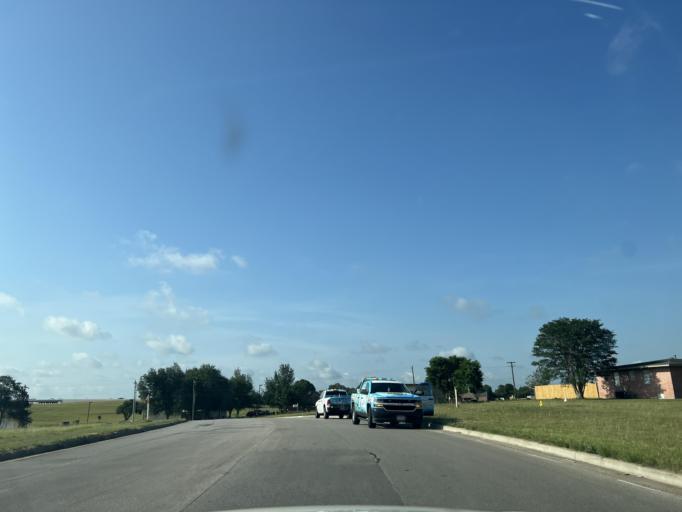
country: US
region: Texas
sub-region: Washington County
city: Brenham
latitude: 30.1479
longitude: -96.3854
